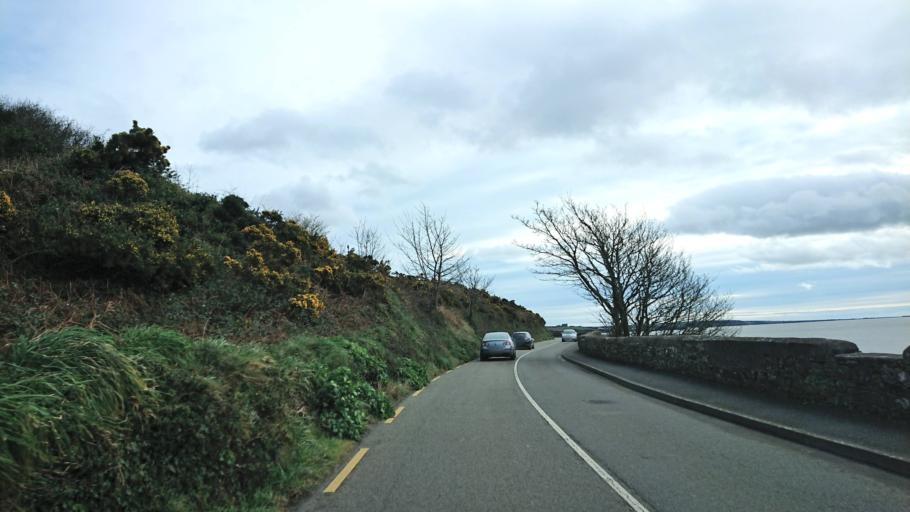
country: IE
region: Munster
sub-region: Waterford
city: Dunmore East
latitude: 52.2434
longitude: -6.9646
